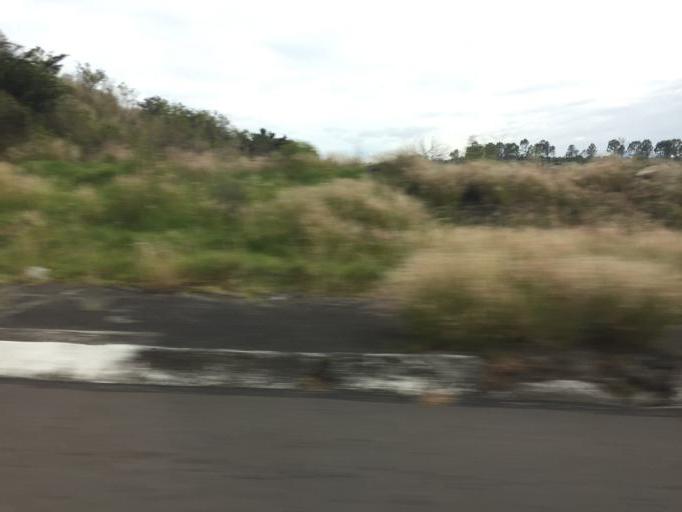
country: MX
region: Mexico
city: Huaniqueo de Morales
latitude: 19.8826
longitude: -101.4968
